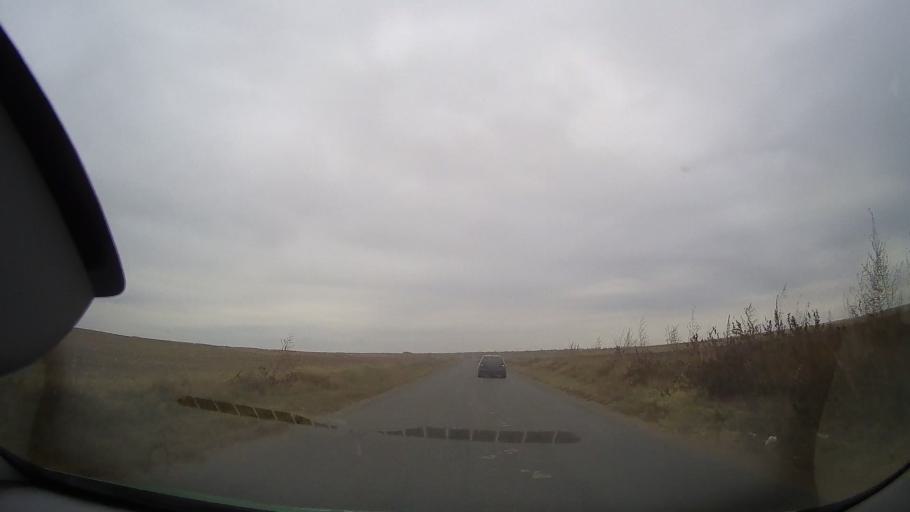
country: RO
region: Buzau
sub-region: Comuna Rusetu
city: Rusetu
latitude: 44.9664
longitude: 27.1982
